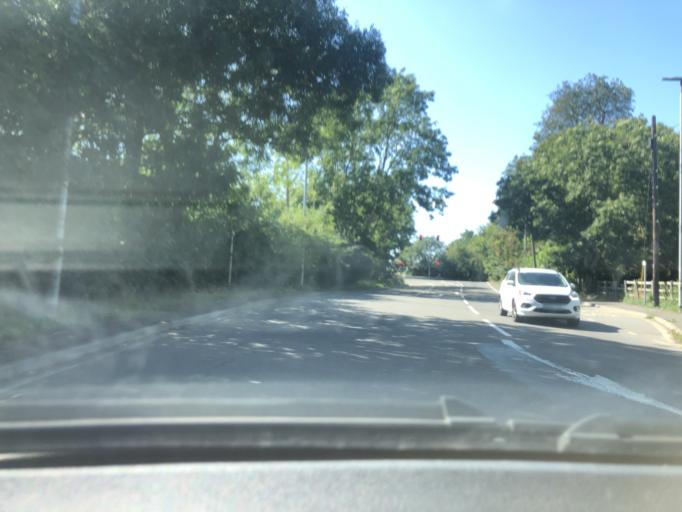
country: GB
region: England
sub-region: Somerset
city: Puriton
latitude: 51.1550
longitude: -2.9572
